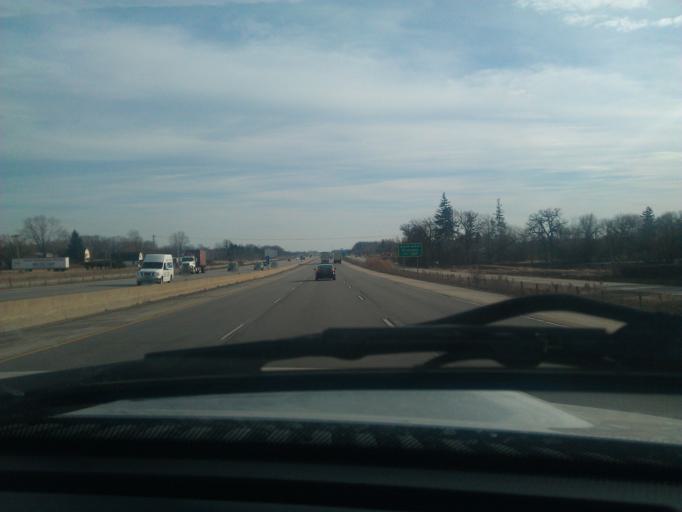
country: US
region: Wisconsin
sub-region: Kenosha County
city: Somers
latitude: 42.6825
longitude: -87.9532
